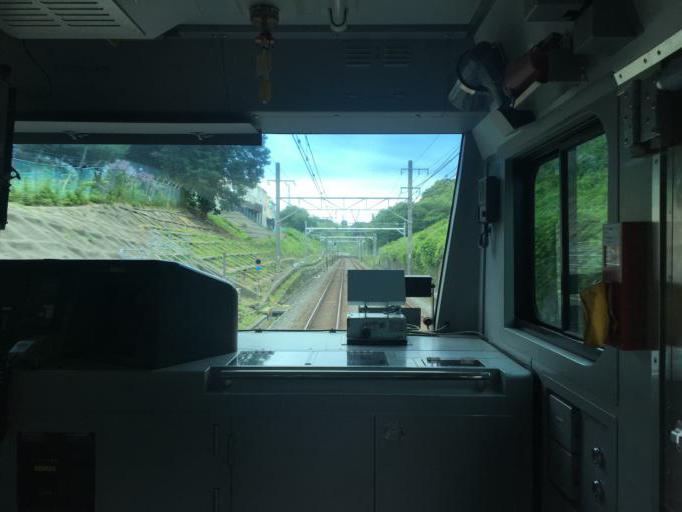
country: JP
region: Kanagawa
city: Yokohama
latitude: 35.4412
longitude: 139.5662
